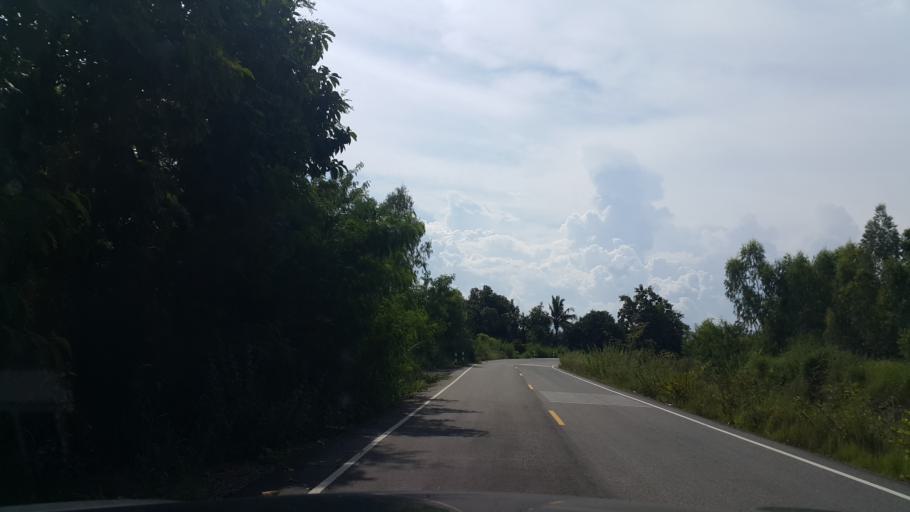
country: TH
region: Chiang Mai
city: Mae On
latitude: 18.8102
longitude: 99.1848
